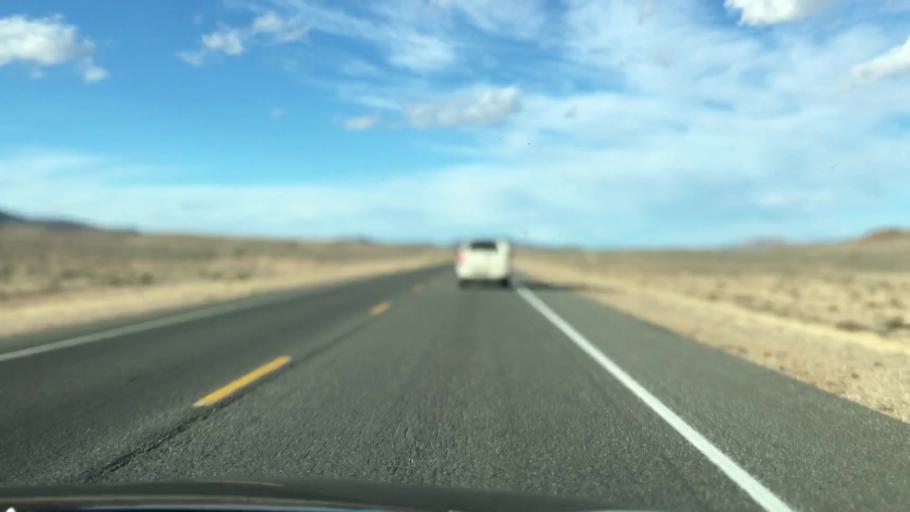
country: US
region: Nevada
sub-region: Esmeralda County
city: Goldfield
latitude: 37.5518
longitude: -117.1977
